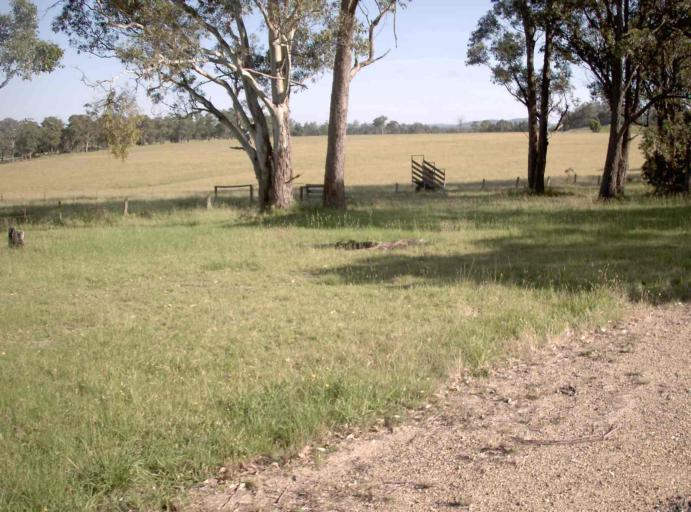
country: AU
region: Victoria
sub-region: East Gippsland
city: Lakes Entrance
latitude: -37.6958
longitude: 148.4660
